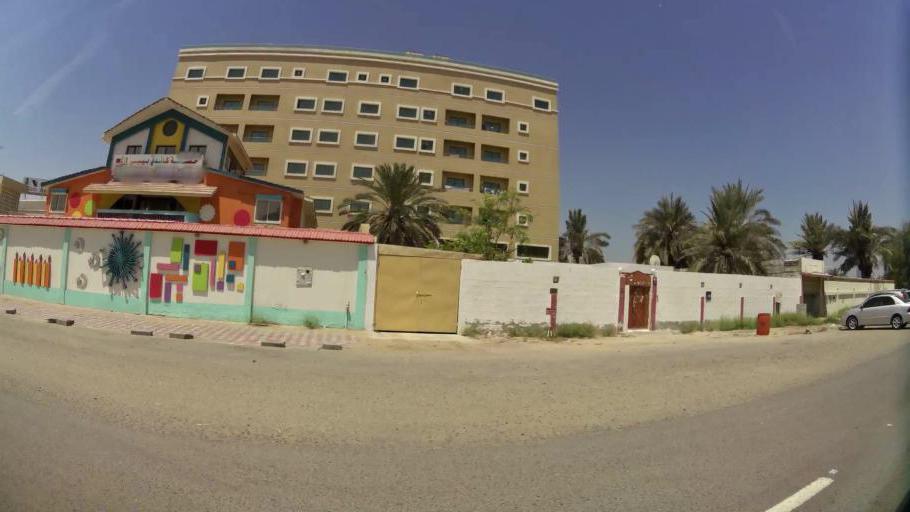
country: AE
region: Ajman
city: Ajman
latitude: 25.3934
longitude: 55.4489
